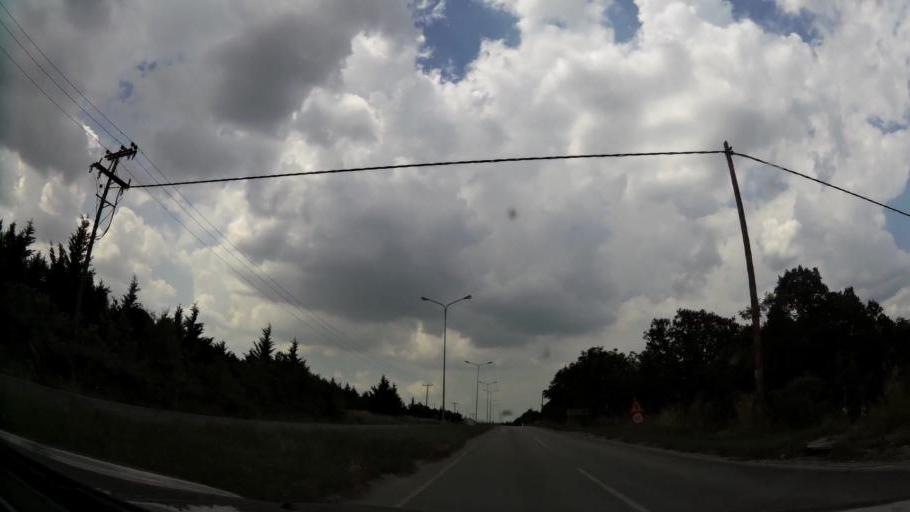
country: GR
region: West Macedonia
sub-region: Nomos Kozanis
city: Koila
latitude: 40.3265
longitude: 21.8275
